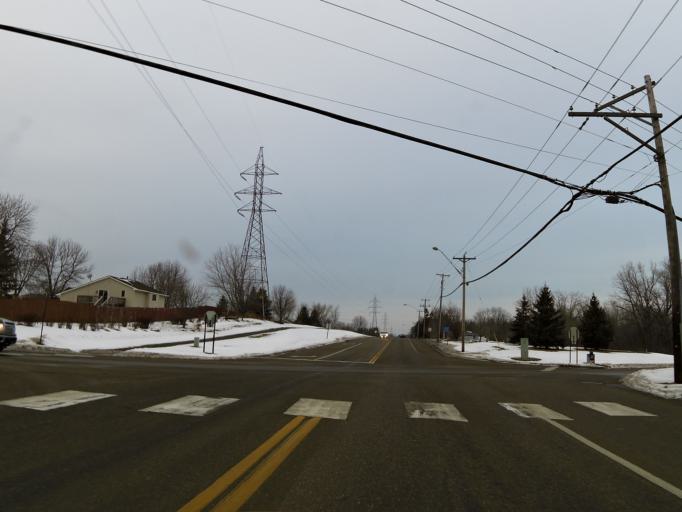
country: US
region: Minnesota
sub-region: Washington County
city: Oakdale
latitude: 44.9854
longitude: -92.9647
